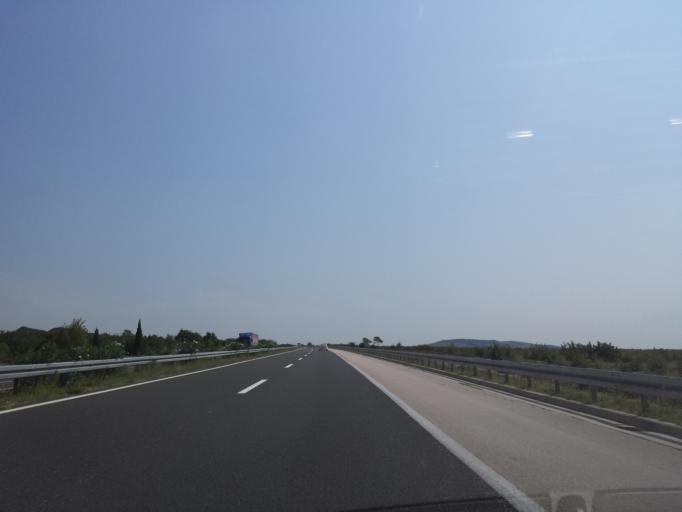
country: HR
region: Zadarska
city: Galovac
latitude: 44.0976
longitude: 15.4732
